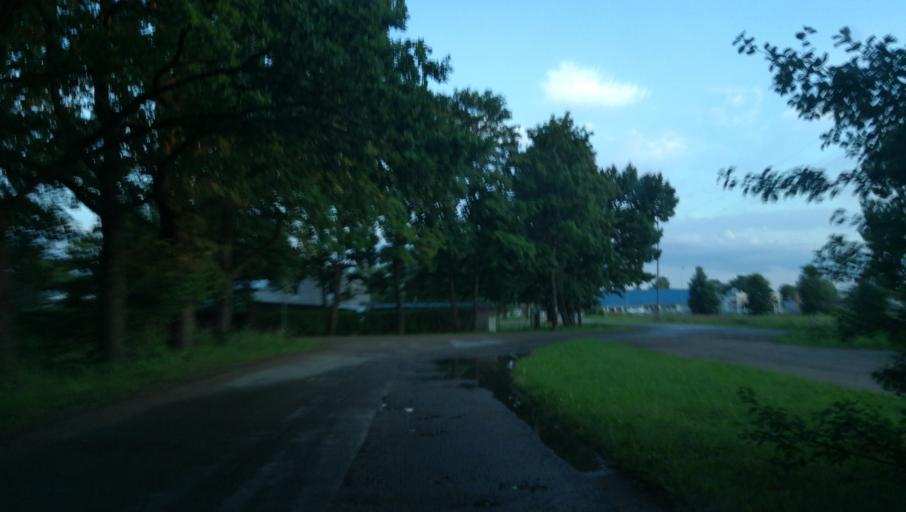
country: LV
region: Cesu Rajons
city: Cesis
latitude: 57.3141
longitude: 25.3010
